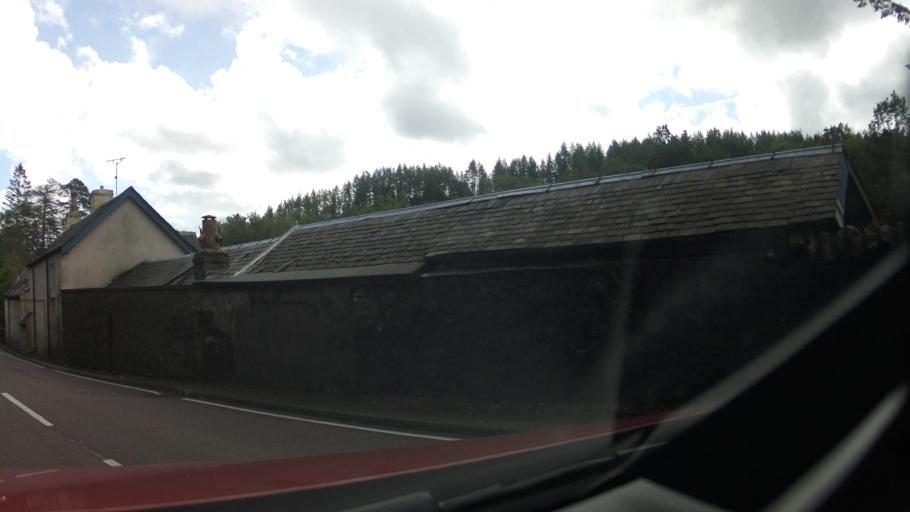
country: GB
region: Scotland
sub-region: Stirling
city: Callander
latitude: 56.2491
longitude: -4.2547
